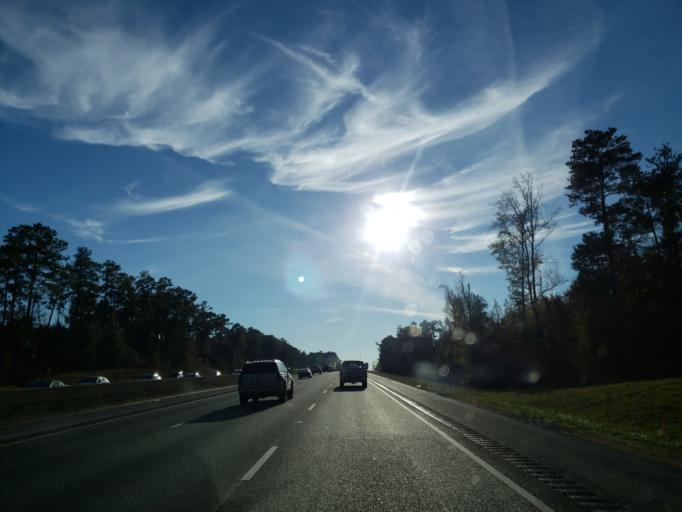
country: US
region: Alabama
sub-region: Tuscaloosa County
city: Vance
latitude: 33.2002
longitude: -87.2340
